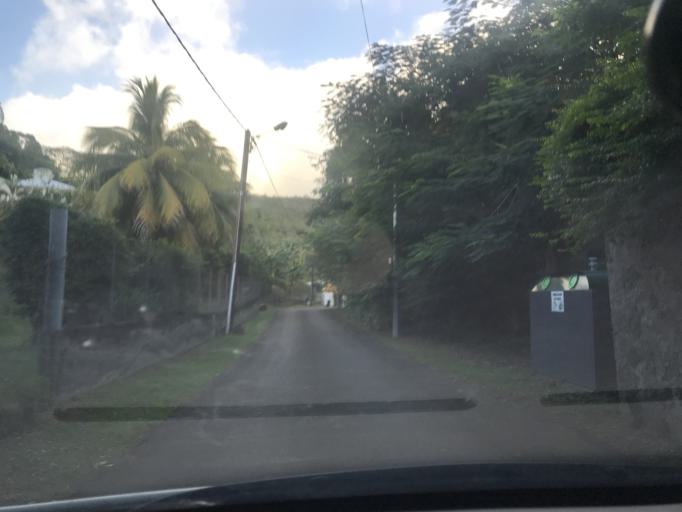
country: MQ
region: Martinique
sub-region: Martinique
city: Fort-de-France
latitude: 14.6341
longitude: -61.1322
